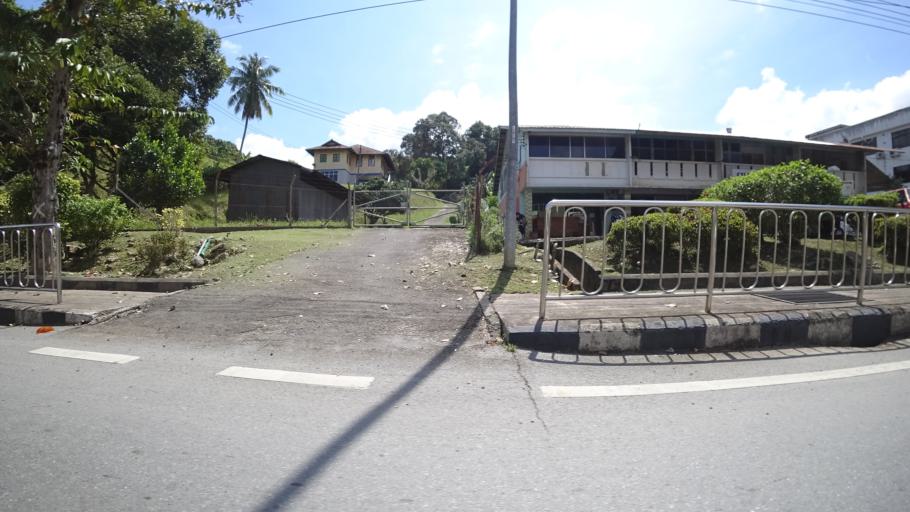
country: MY
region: Sarawak
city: Limbang
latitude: 4.7557
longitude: 115.0111
